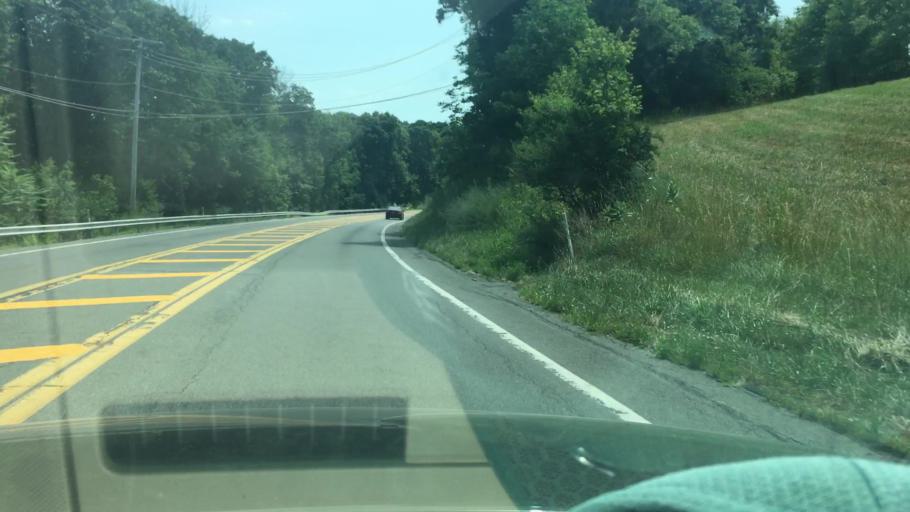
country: US
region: Pennsylvania
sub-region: Schuylkill County
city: Coaldale
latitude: 40.7521
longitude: -75.9080
